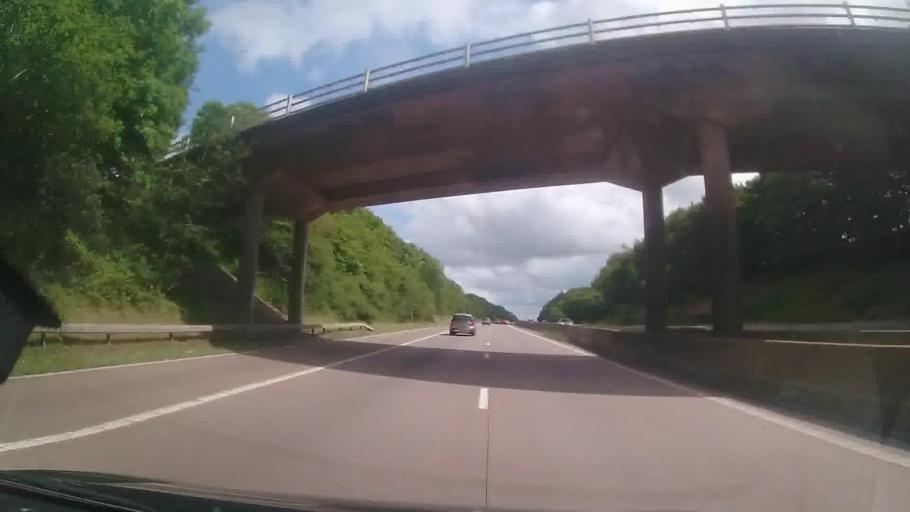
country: GB
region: England
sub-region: Shropshire
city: Shifnal
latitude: 52.6760
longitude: -2.3578
